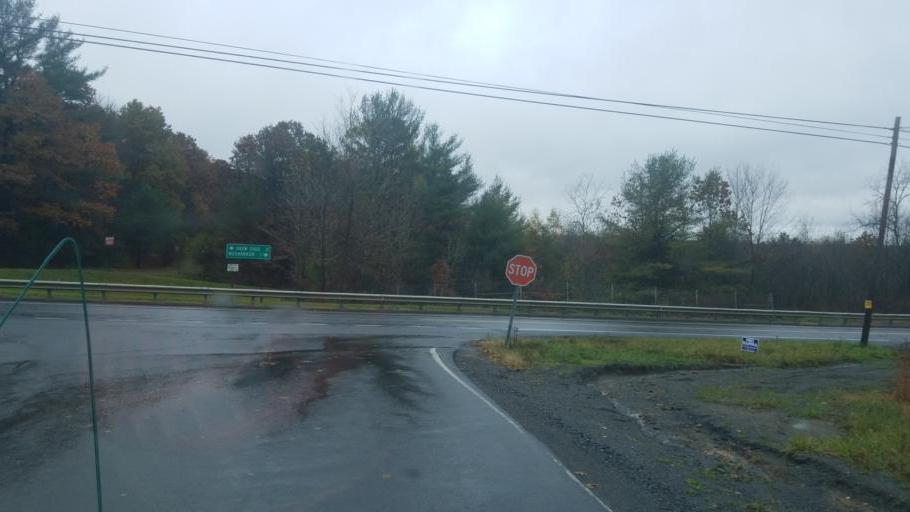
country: US
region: Pennsylvania
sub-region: Centre County
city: Milesburg
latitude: 41.0328
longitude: -77.9911
